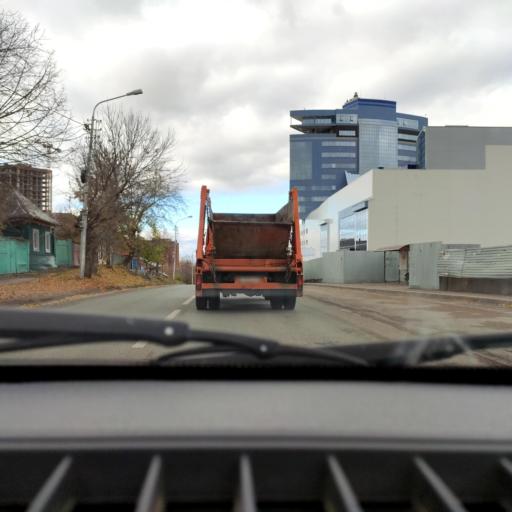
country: RU
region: Bashkortostan
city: Ufa
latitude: 54.7475
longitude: 55.9677
